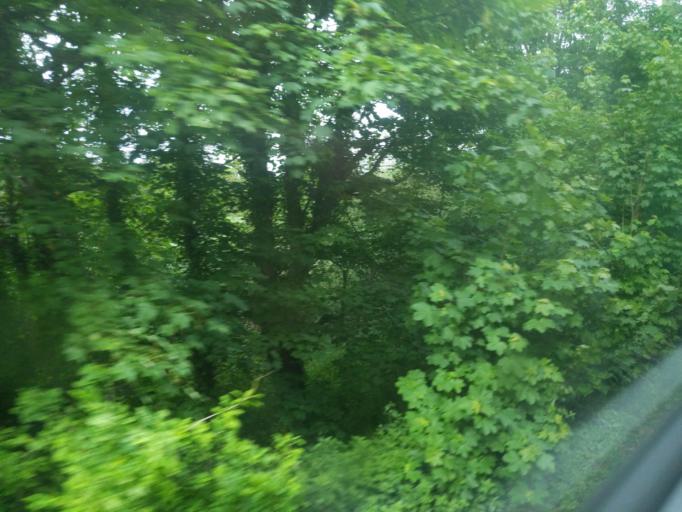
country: GB
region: England
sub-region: Devon
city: Crediton
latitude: 50.7800
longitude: -3.6280
